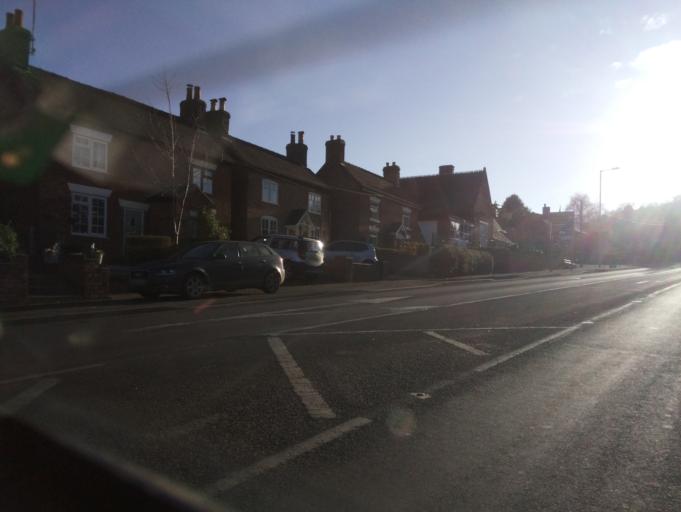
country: GB
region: England
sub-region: Staffordshire
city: Barton under Needwood
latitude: 52.8528
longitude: -1.7707
